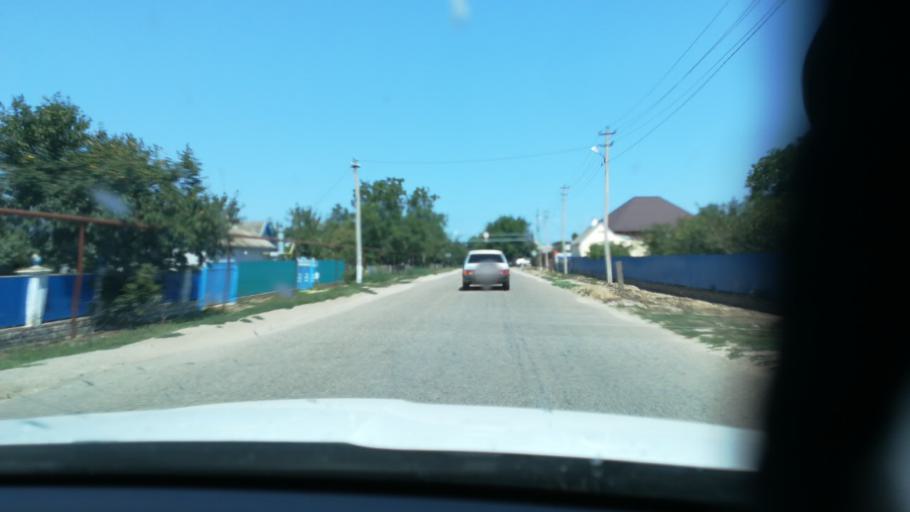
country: RU
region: Krasnodarskiy
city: Starotitarovskaya
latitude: 45.2127
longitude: 37.1442
